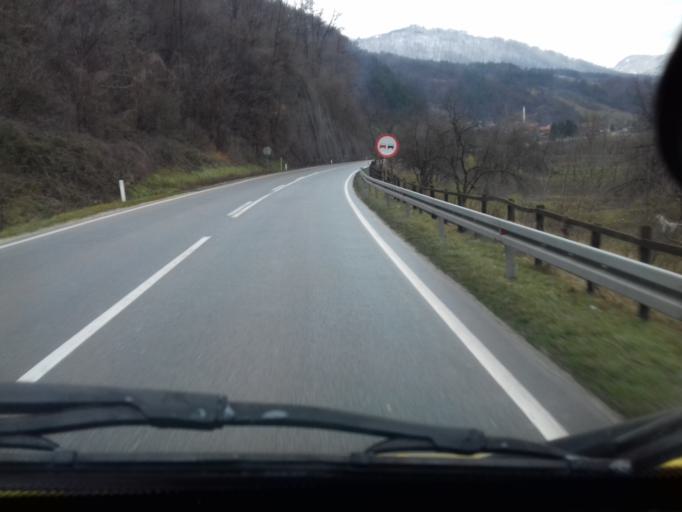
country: BA
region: Federation of Bosnia and Herzegovina
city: Zeljezno Polje
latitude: 44.3377
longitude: 17.9227
